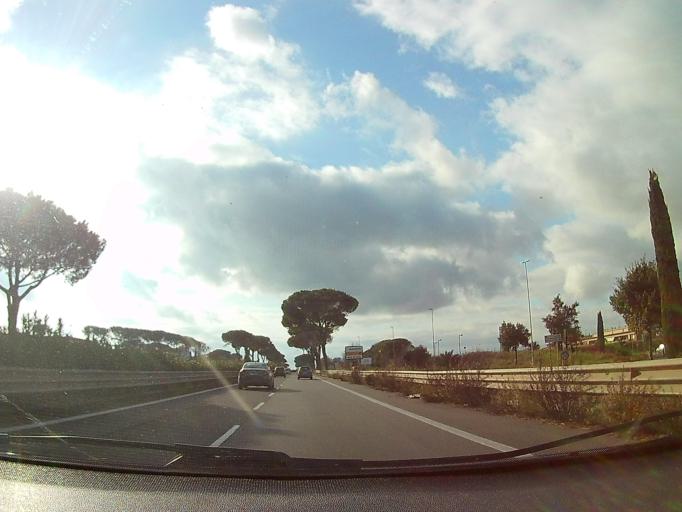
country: IT
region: Latium
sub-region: Citta metropolitana di Roma Capitale
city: Vitinia
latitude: 41.7948
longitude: 12.4341
